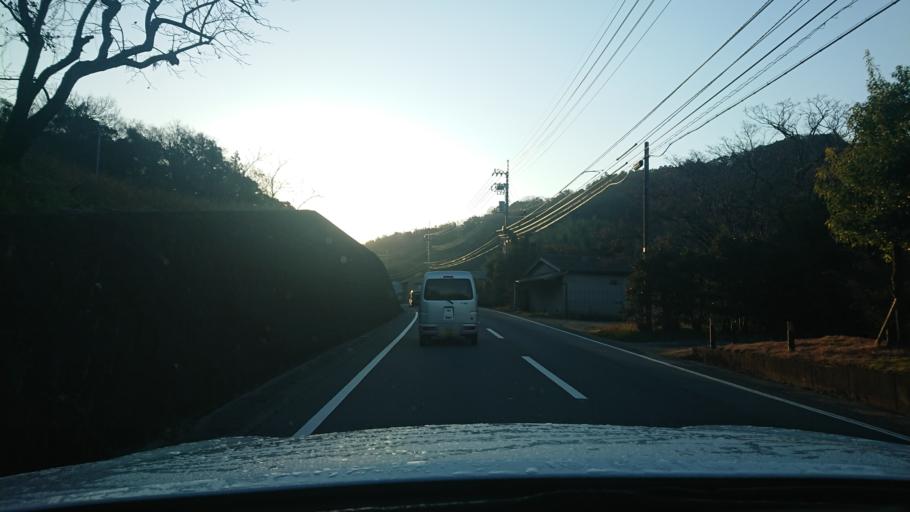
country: JP
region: Tokushima
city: Komatsushimacho
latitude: 33.9484
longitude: 134.5676
